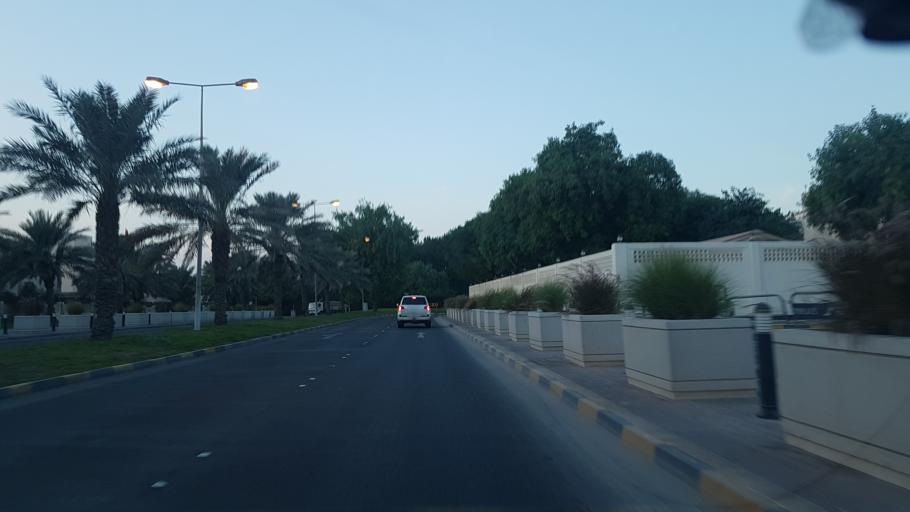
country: BH
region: Northern
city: Ar Rifa'
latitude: 26.1232
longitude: 50.5357
